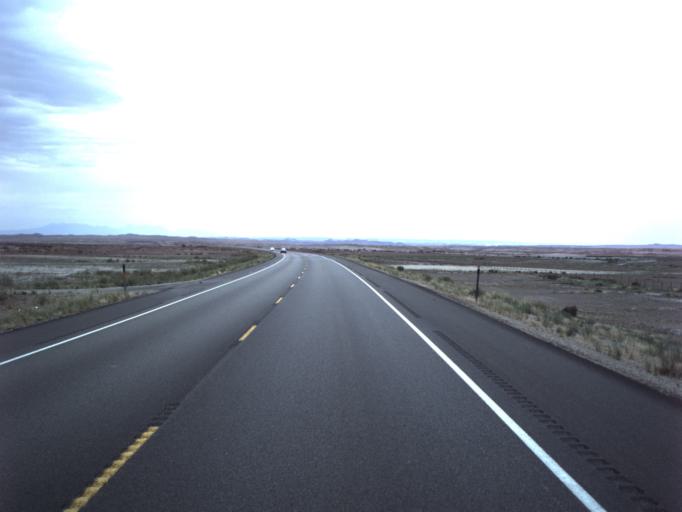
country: US
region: Utah
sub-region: Carbon County
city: East Carbon City
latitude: 39.0059
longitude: -110.2767
